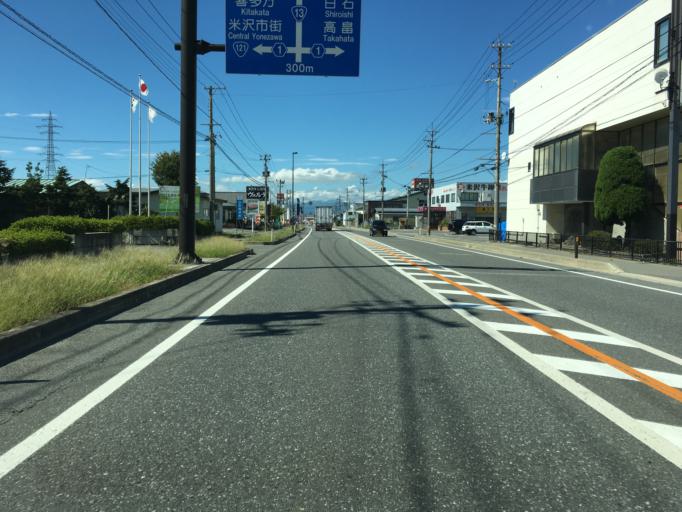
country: JP
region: Yamagata
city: Yonezawa
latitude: 37.9180
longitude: 140.1317
